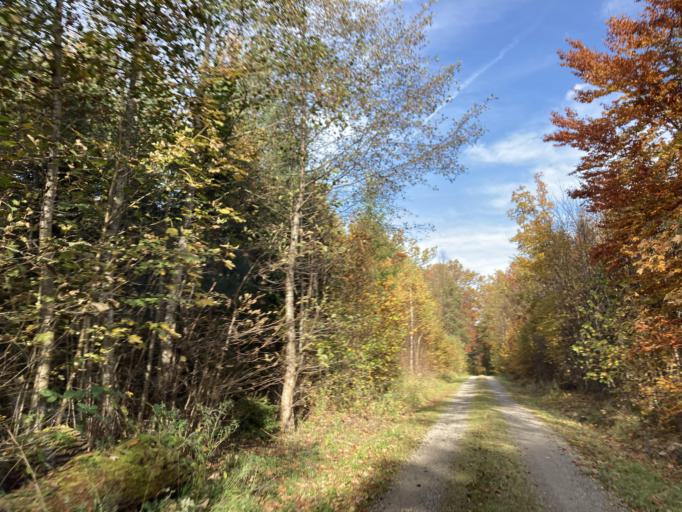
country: DE
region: Baden-Wuerttemberg
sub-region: Tuebingen Region
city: Bodelshausen
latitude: 48.4364
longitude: 8.9673
